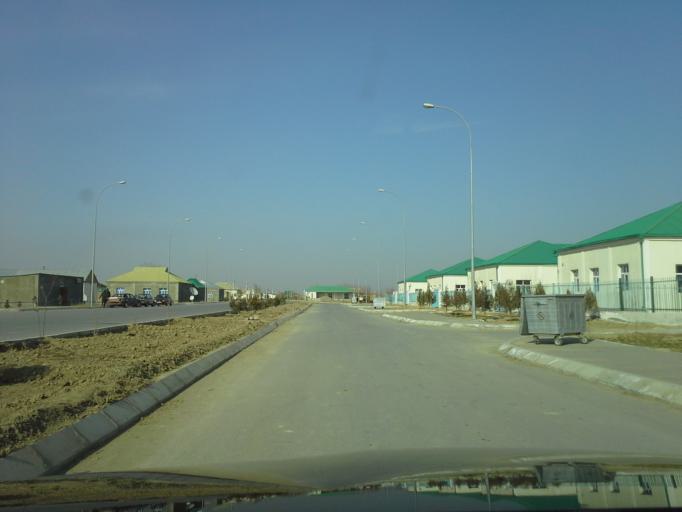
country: TM
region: Ahal
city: Abadan
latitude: 38.1736
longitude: 58.0476
